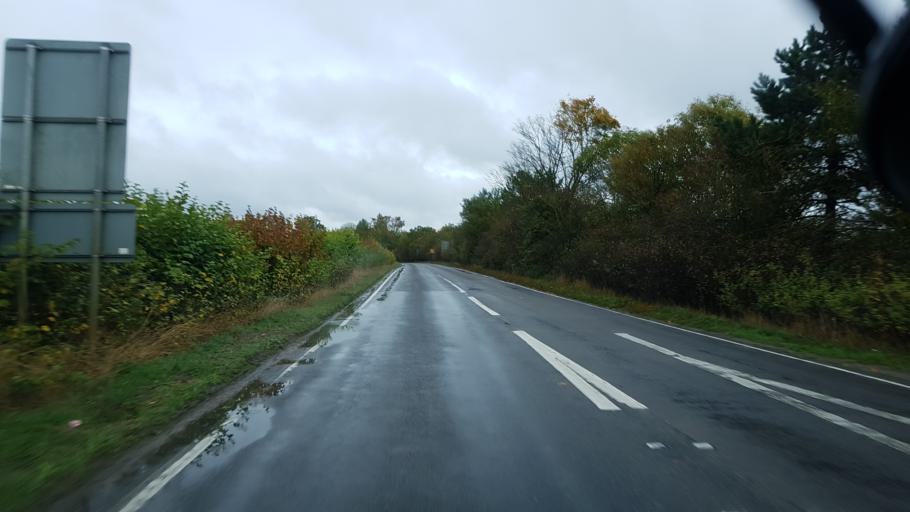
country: GB
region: England
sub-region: Oxfordshire
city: Ducklington
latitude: 51.7501
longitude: -1.4553
